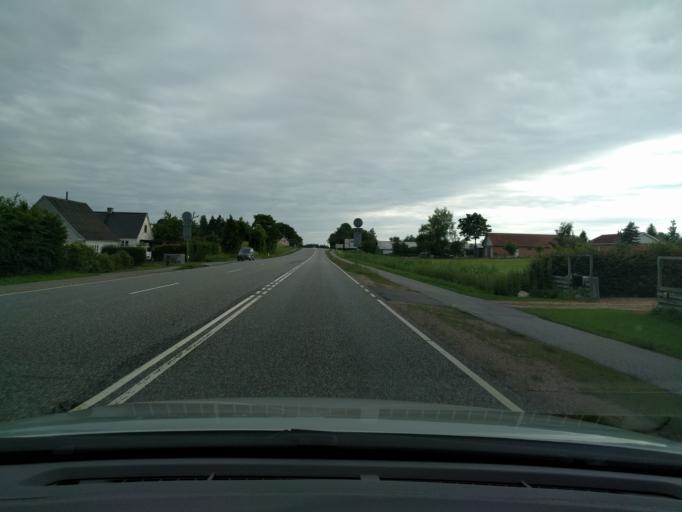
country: DK
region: Zealand
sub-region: Lejre Kommune
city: Osted
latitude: 55.5101
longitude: 11.8896
